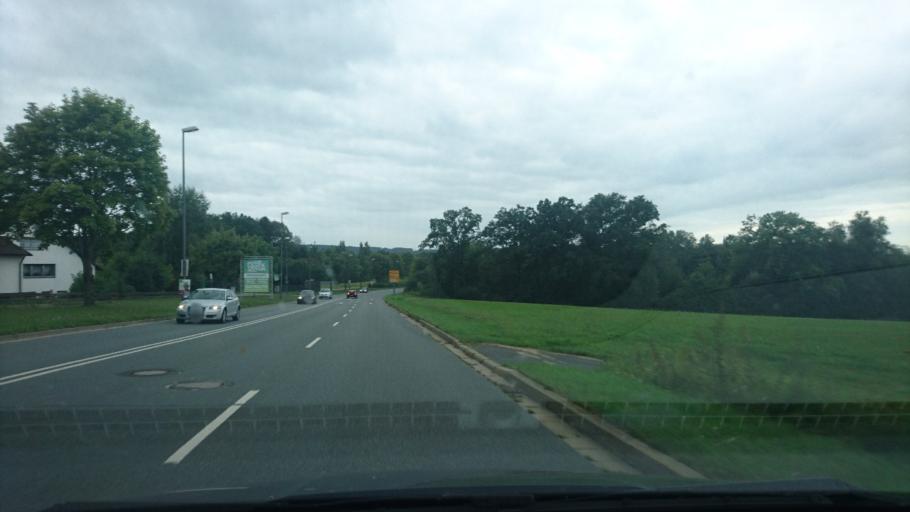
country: DE
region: Bavaria
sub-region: Upper Franconia
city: Bayreuth
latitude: 49.9273
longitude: 11.5953
